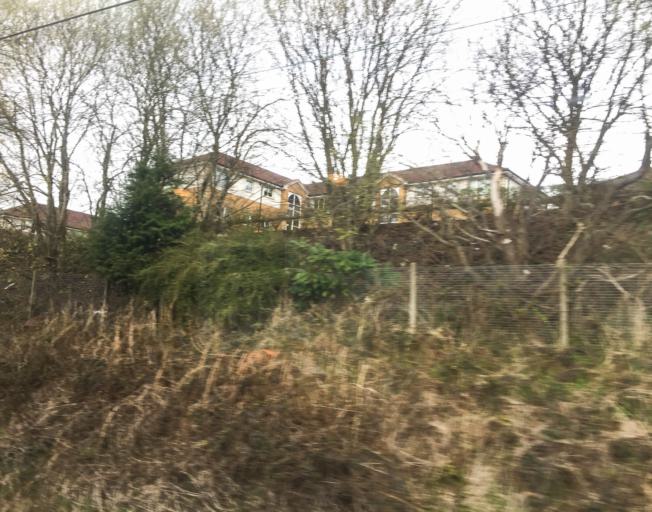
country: GB
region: Scotland
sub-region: West Dunbartonshire
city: Clydebank
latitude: 55.9088
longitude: -4.4111
